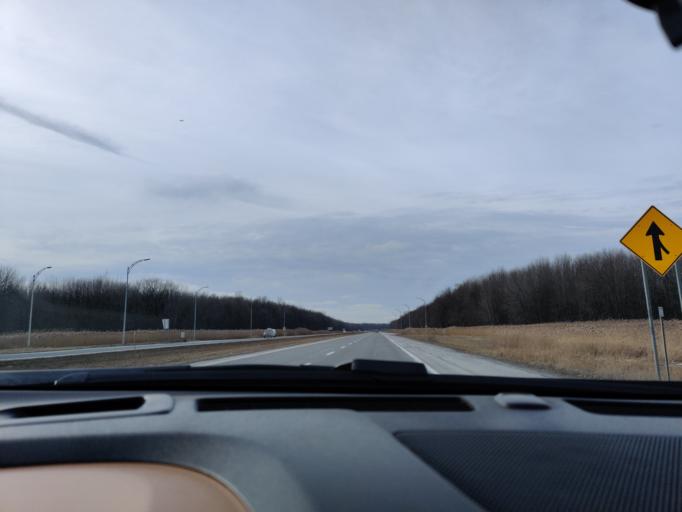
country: CA
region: Quebec
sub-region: Monteregie
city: Les Coteaux
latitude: 45.2345
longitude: -74.2902
